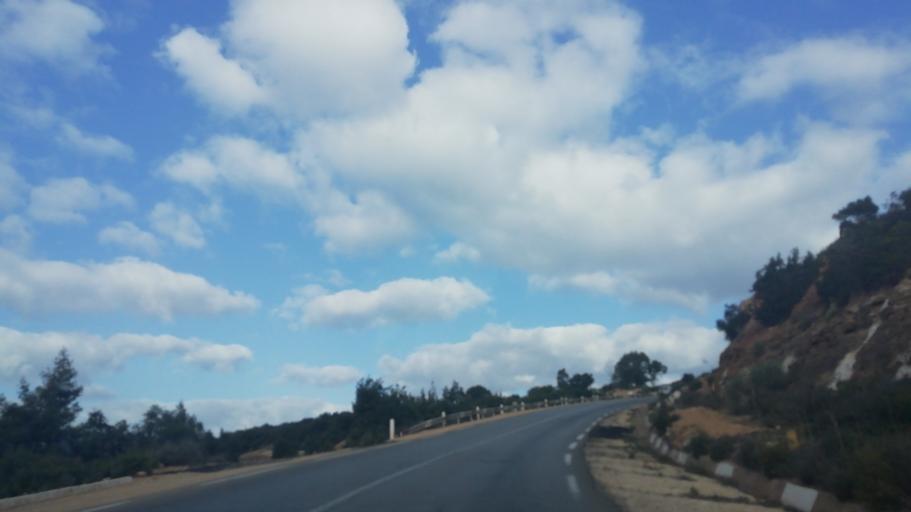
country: DZ
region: Relizane
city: Mazouna
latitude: 36.2424
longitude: 0.5374
